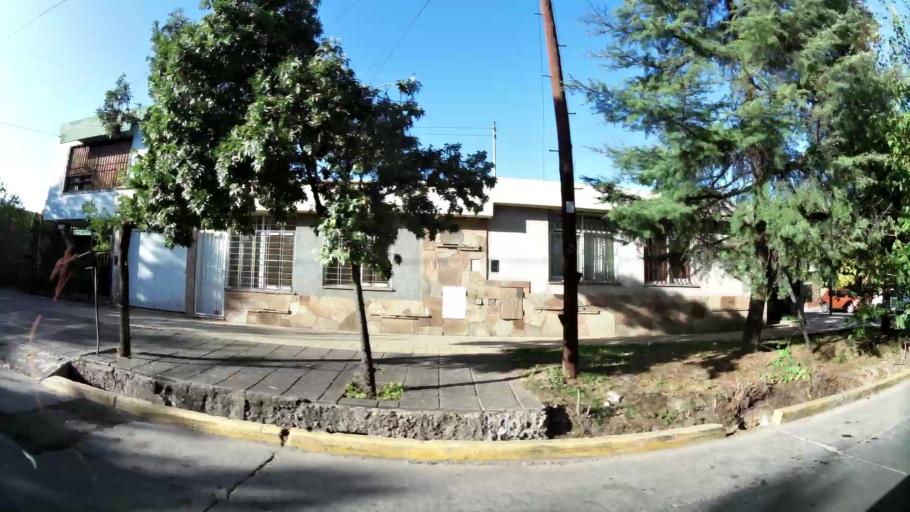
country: AR
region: Mendoza
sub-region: Departamento de Godoy Cruz
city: Godoy Cruz
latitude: -32.9264
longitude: -68.8412
